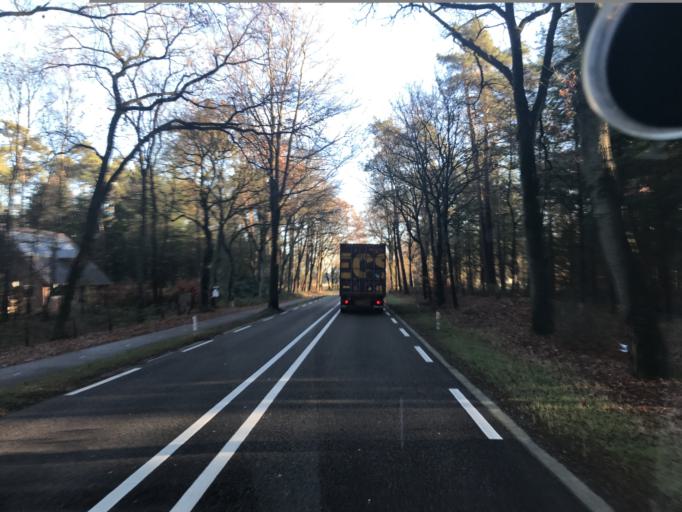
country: NL
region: Gelderland
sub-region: Gemeente Ermelo
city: Ermelo
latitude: 52.3153
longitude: 5.6695
